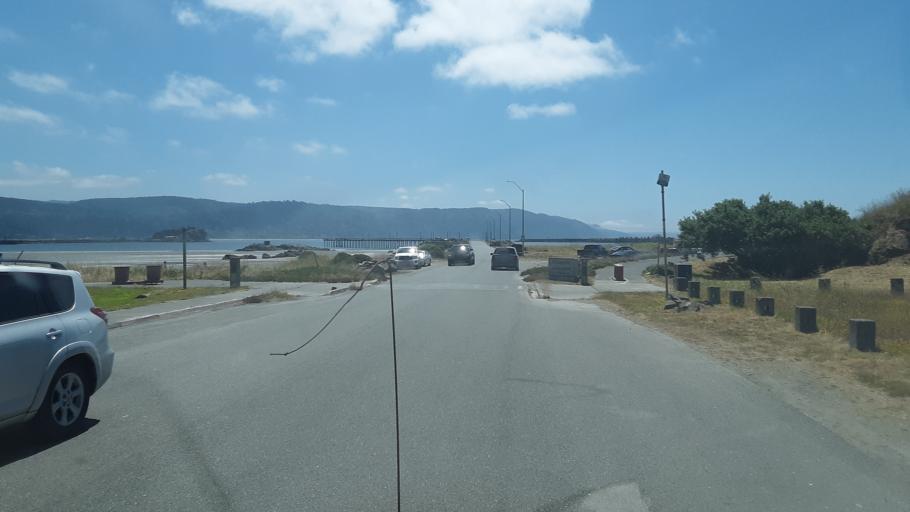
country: US
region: California
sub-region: Del Norte County
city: Crescent City
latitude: 41.7466
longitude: -124.2008
